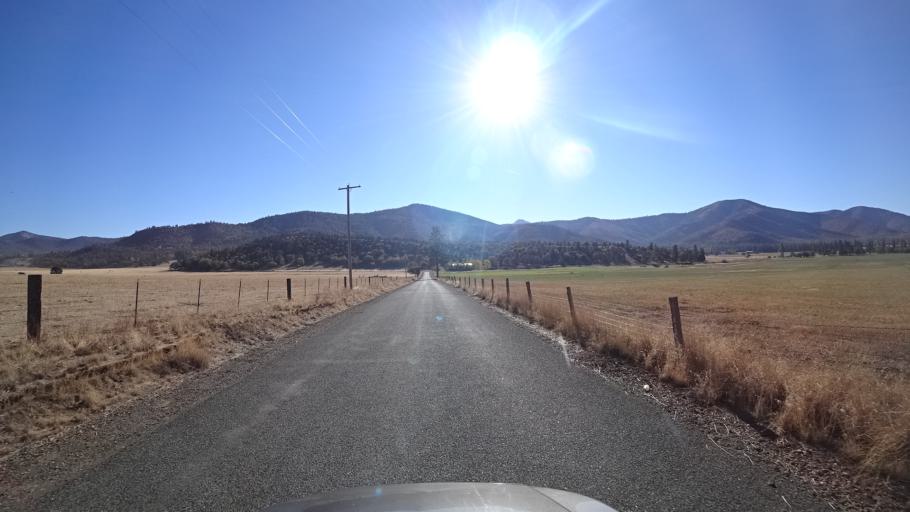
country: US
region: California
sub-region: Siskiyou County
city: Yreka
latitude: 41.5810
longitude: -122.7932
